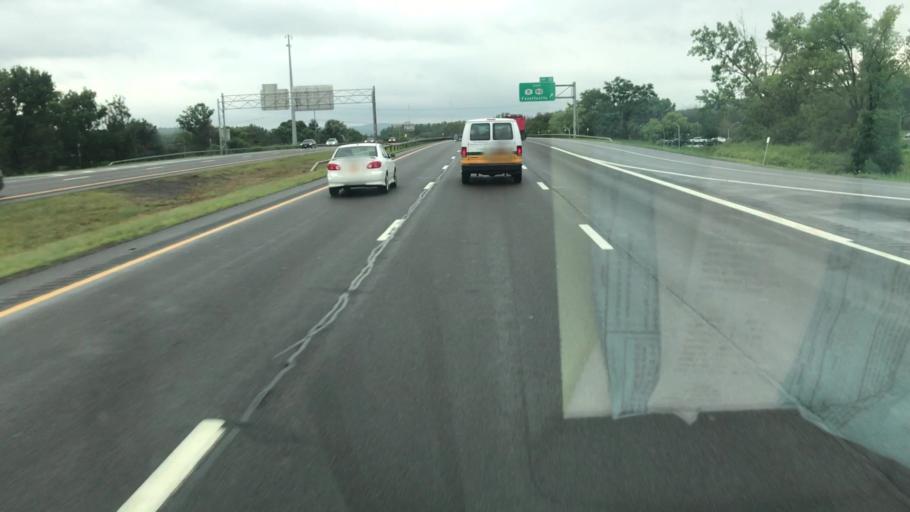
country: US
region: New York
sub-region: Onondaga County
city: East Syracuse
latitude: 43.0355
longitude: -76.0580
